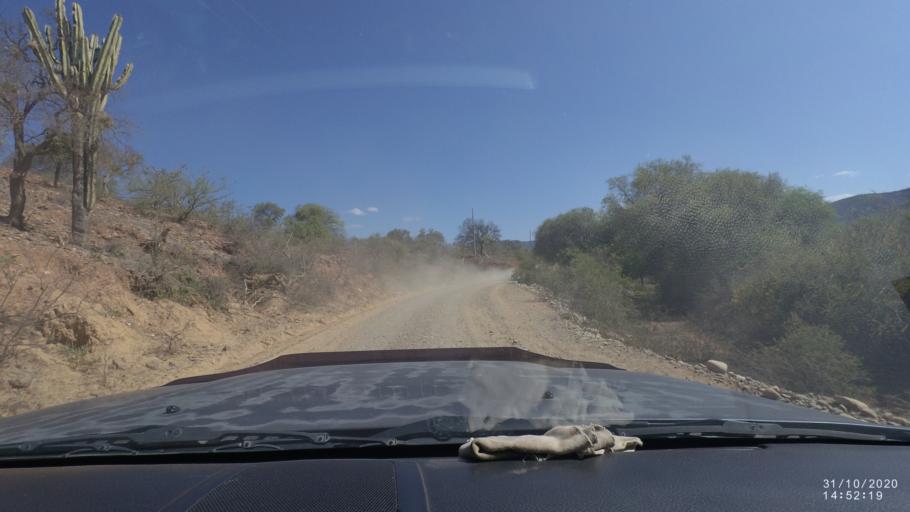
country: BO
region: Cochabamba
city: Aiquile
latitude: -18.2129
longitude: -64.8564
